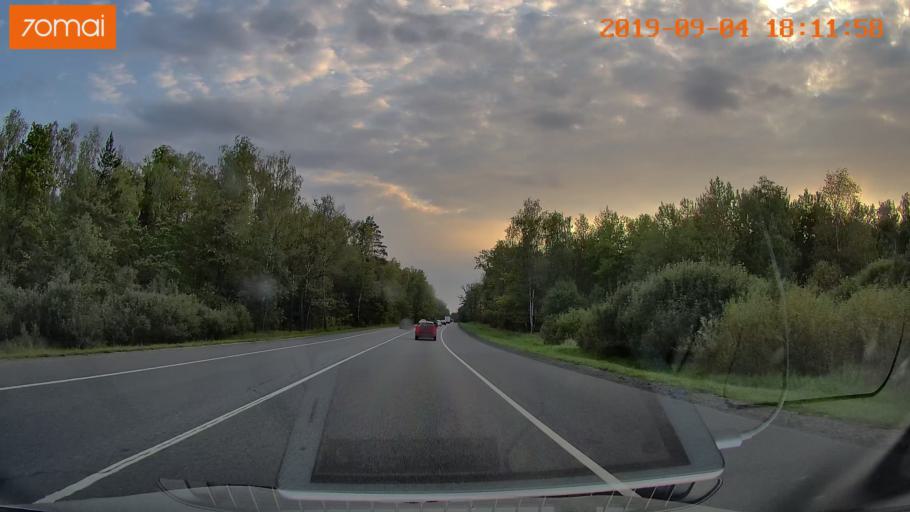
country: RU
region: Moskovskaya
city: Lopatinskiy
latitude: 55.3735
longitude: 38.7484
